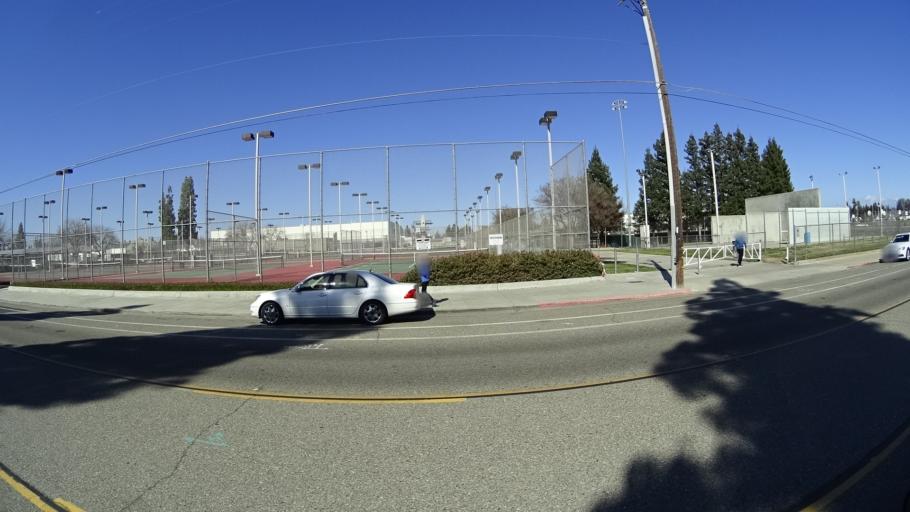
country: US
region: California
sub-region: Fresno County
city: Clovis
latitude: 36.8592
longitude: -119.7627
